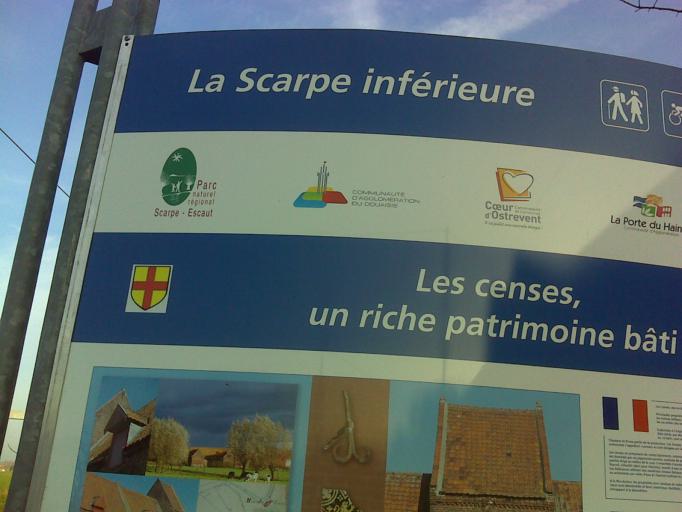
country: FR
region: Nord-Pas-de-Calais
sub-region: Departement du Nord
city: Wandignies-Hamage
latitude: 50.4082
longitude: 3.3338
